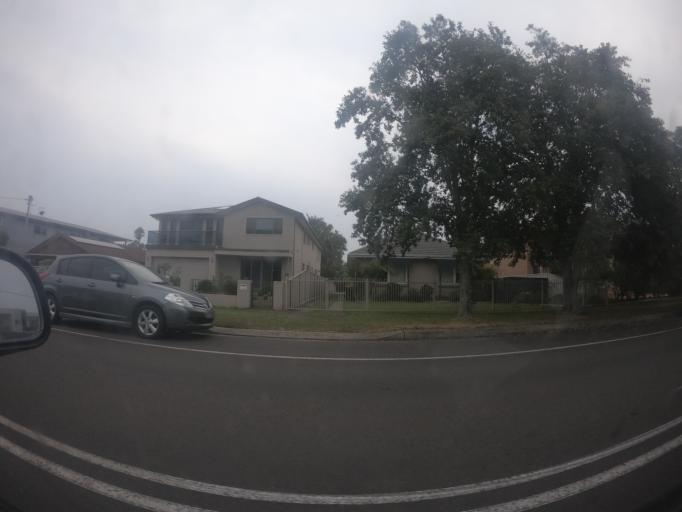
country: AU
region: New South Wales
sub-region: Shellharbour
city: Barrack Heights
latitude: -34.5642
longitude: 150.8669
